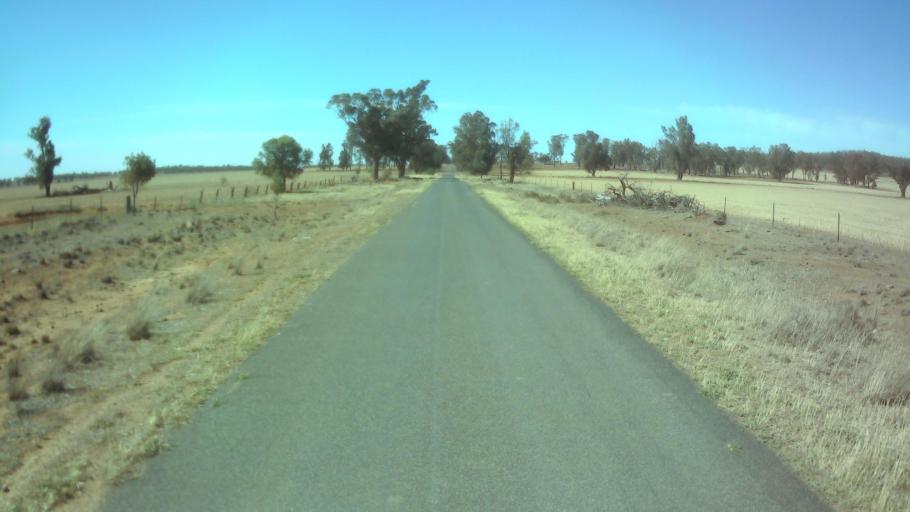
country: AU
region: New South Wales
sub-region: Forbes
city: Forbes
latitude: -33.7360
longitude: 147.7418
